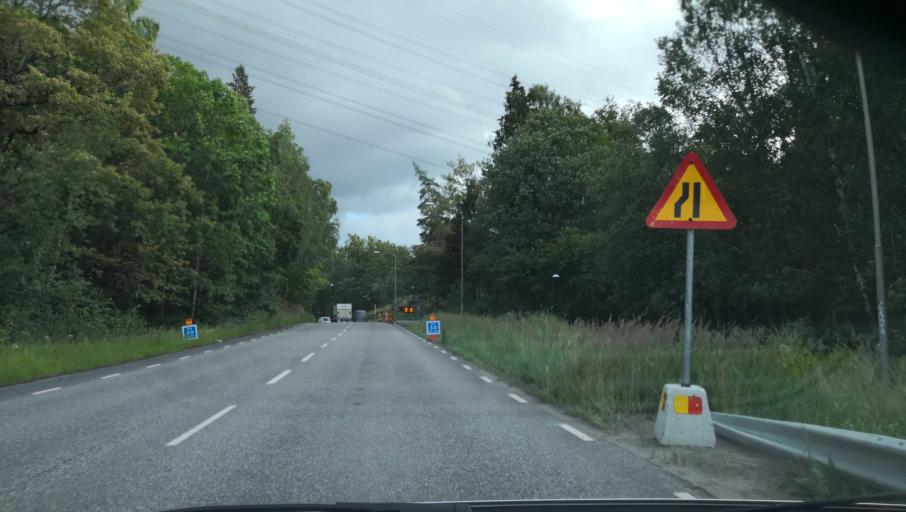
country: SE
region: Stockholm
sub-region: Stockholms Kommun
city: Arsta
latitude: 59.2532
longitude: 18.0488
